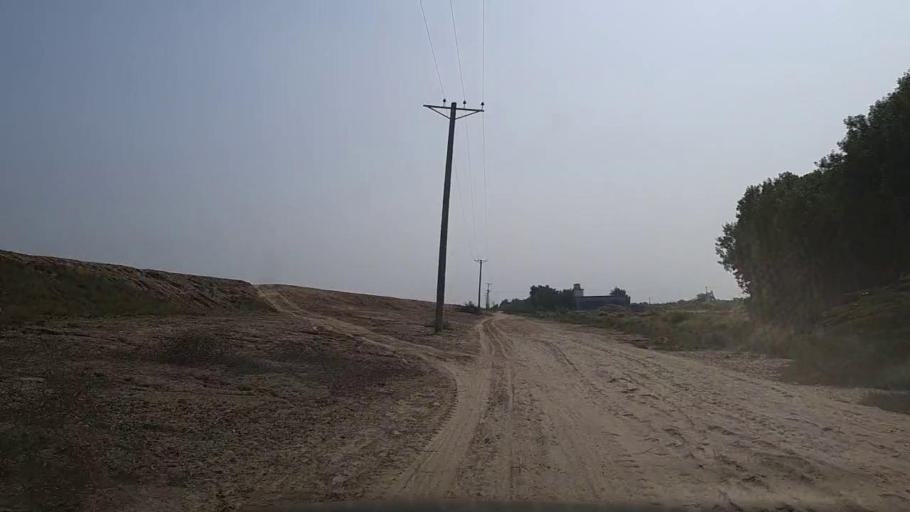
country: PK
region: Sindh
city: Chuhar Jamali
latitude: 24.5593
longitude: 67.9148
